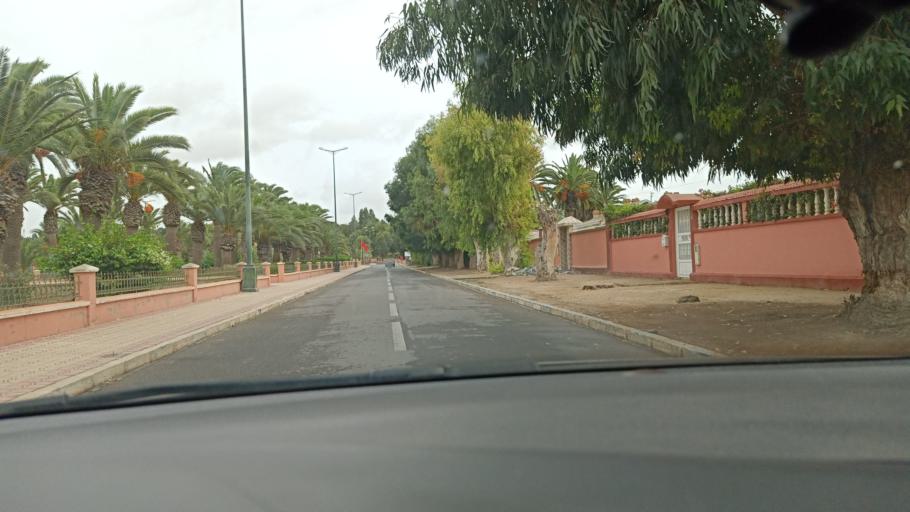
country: MA
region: Doukkala-Abda
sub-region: Safi
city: Youssoufia
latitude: 32.2448
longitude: -8.5298
